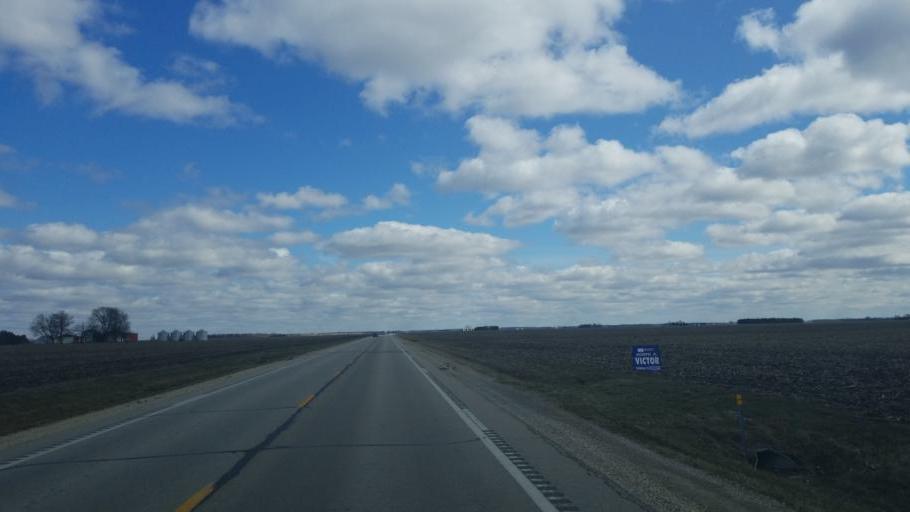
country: US
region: Illinois
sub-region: Douglas County
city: Villa Grove
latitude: 39.7919
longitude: -88.1278
